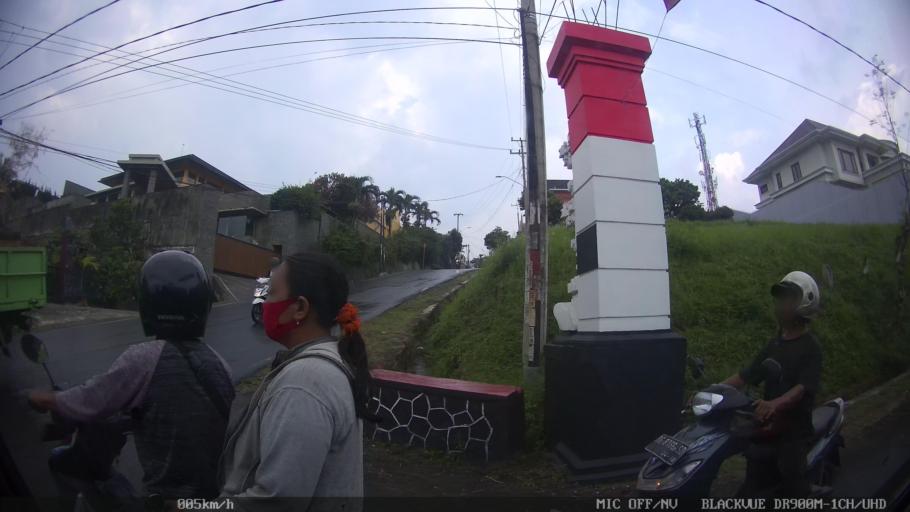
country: ID
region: Lampung
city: Bandarlampung
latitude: -5.4373
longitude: 105.2831
